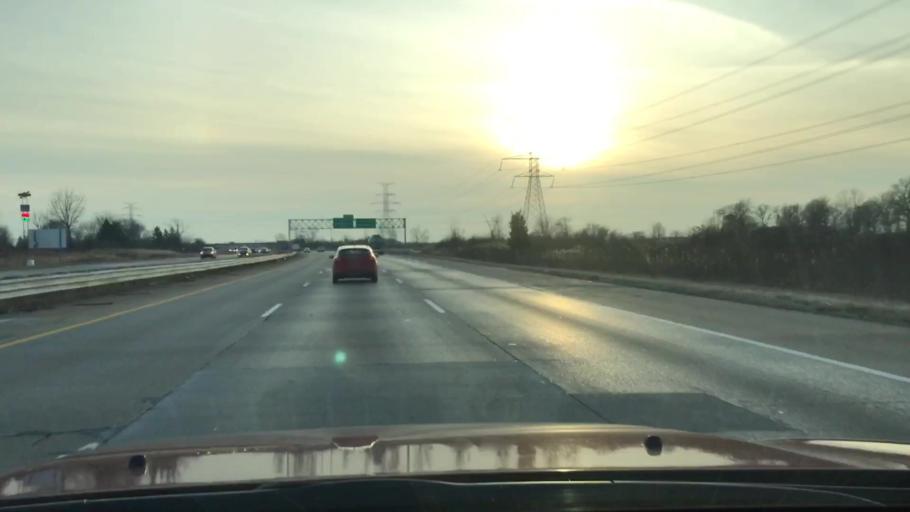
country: US
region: Michigan
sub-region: Monroe County
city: Luna Pier
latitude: 41.8146
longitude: -83.4462
